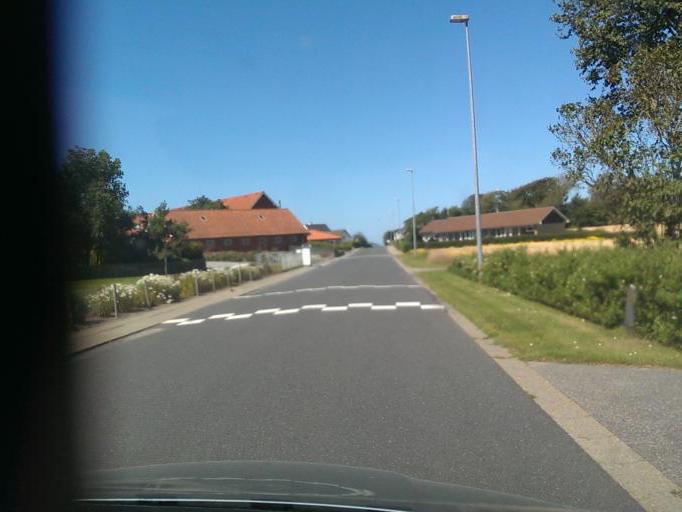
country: DK
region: North Denmark
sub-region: Jammerbugt Kommune
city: Pandrup
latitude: 57.3124
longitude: 9.7155
